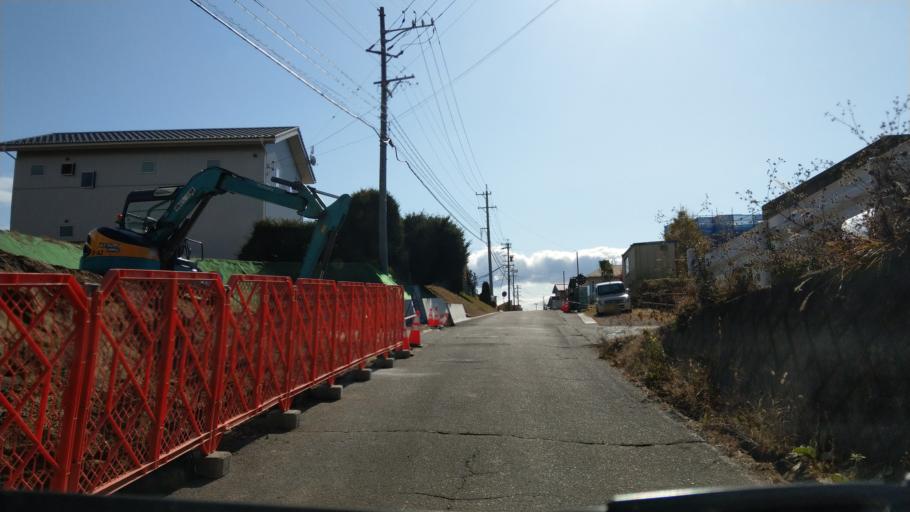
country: JP
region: Nagano
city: Komoro
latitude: 36.3086
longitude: 138.4692
